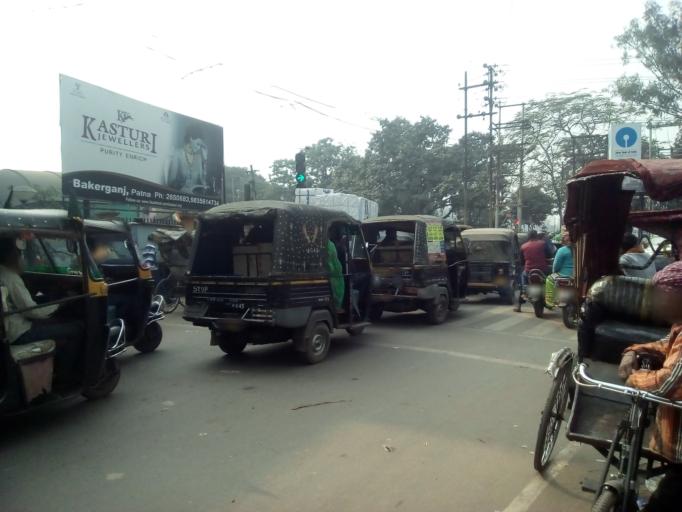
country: IN
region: Bihar
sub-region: Patna
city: Patna
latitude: 25.6160
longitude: 85.1487
